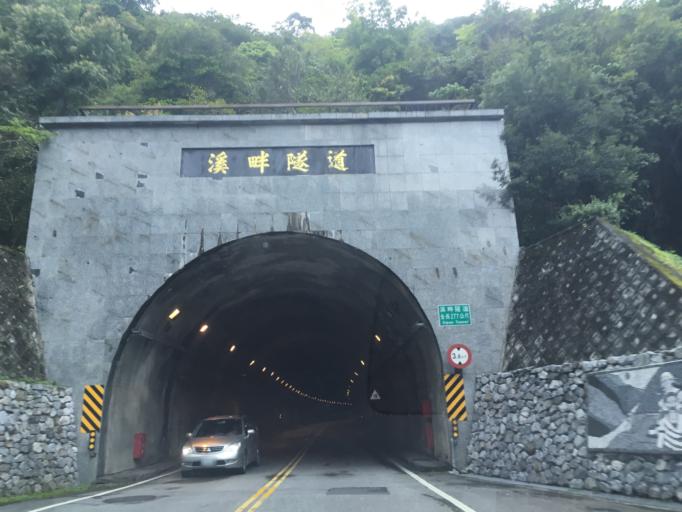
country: TW
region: Taiwan
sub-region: Hualien
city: Hualian
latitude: 24.1719
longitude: 121.5762
